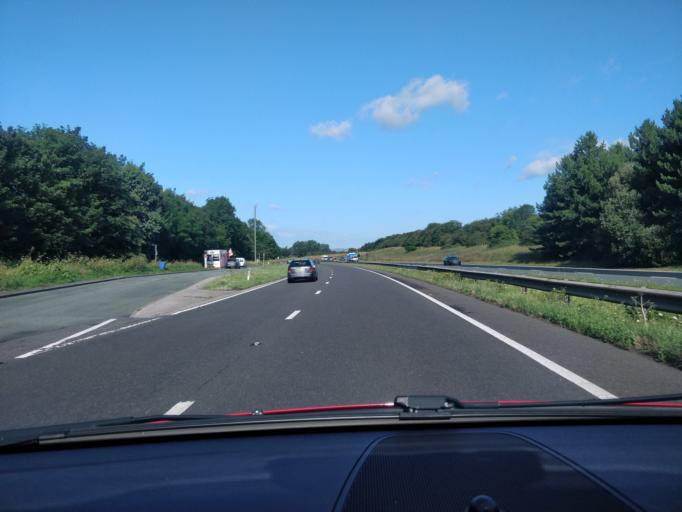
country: GB
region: Wales
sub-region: Conwy
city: Llysfaen
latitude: 53.2914
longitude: -3.6325
